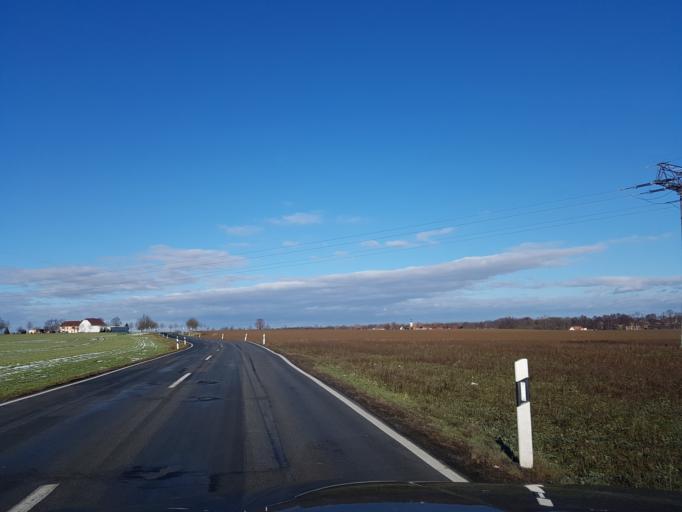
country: DE
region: Saxony
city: Priestewitz
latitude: 51.2378
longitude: 13.5536
